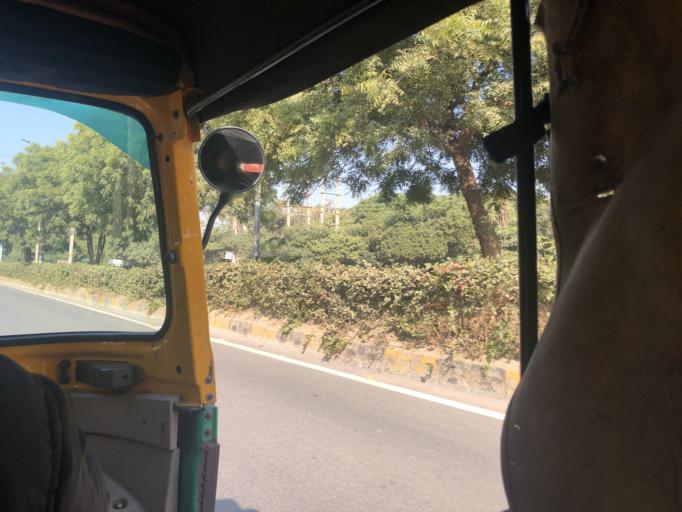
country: IN
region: Haryana
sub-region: Gurgaon
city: Gurgaon
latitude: 28.4447
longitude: 77.0824
